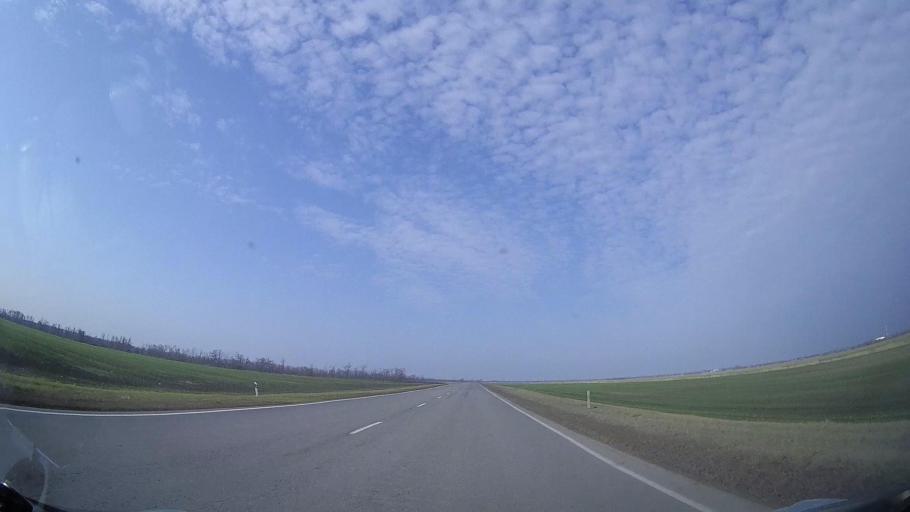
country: RU
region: Rostov
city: Tselina
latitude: 46.5134
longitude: 41.0495
